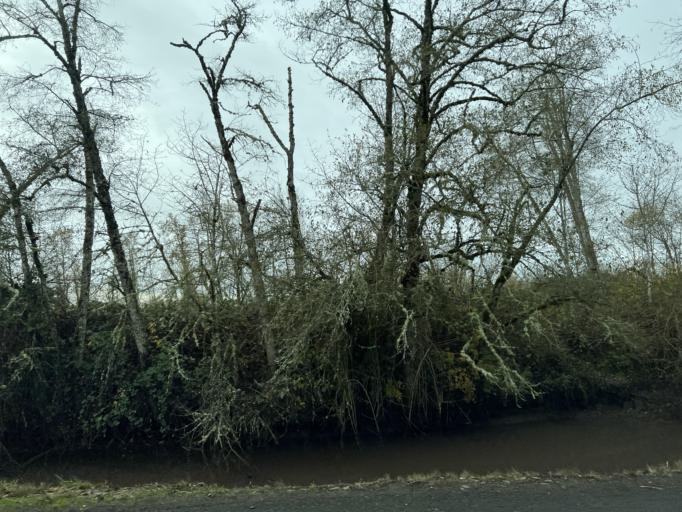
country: US
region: Oregon
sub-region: Polk County
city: Independence
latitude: 44.8014
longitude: -123.0886
